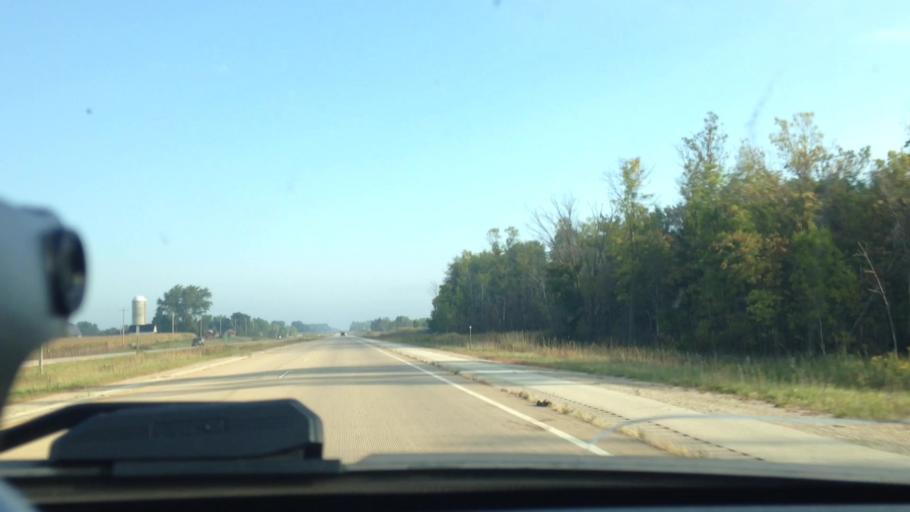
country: US
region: Wisconsin
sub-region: Oconto County
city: Oconto Falls
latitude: 45.0026
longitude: -88.0450
